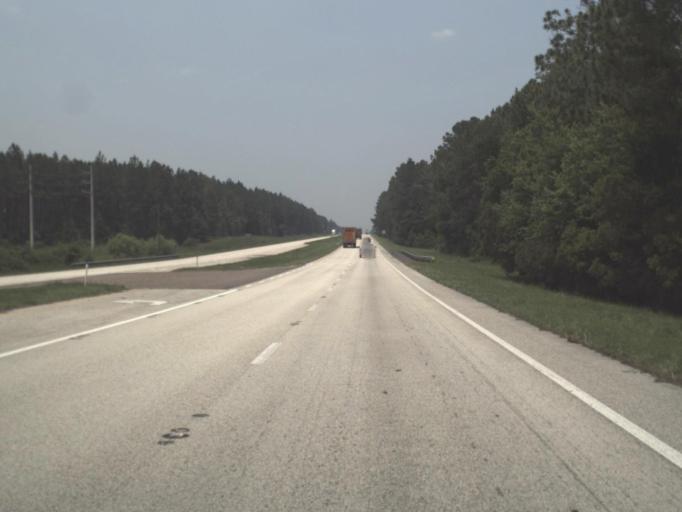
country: US
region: Florida
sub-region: Baker County
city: Macclenny
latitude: 30.1420
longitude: -82.0364
